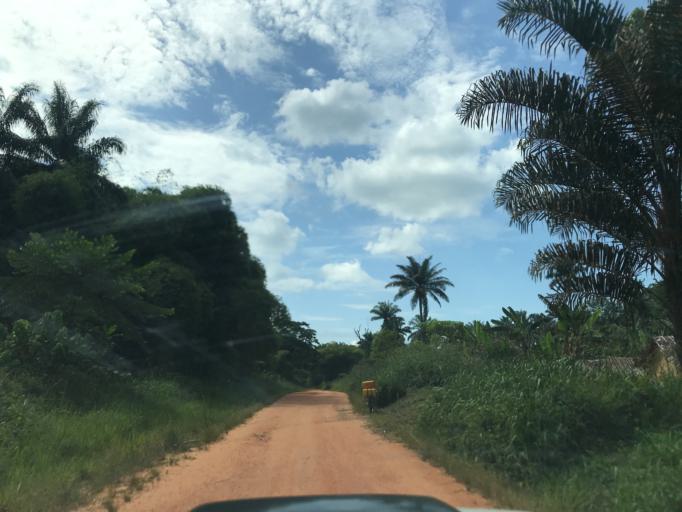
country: CD
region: Eastern Province
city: Kisangani
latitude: 1.0568
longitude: 25.2752
